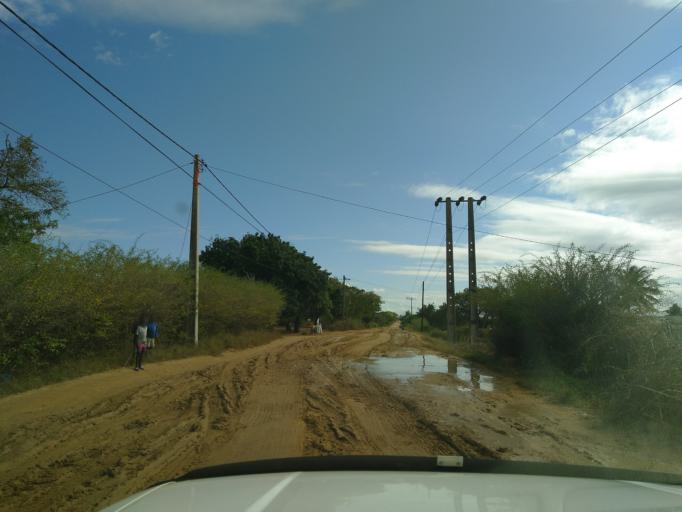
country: MZ
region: Maputo City
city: Maputo
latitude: -26.0025
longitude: 32.5443
